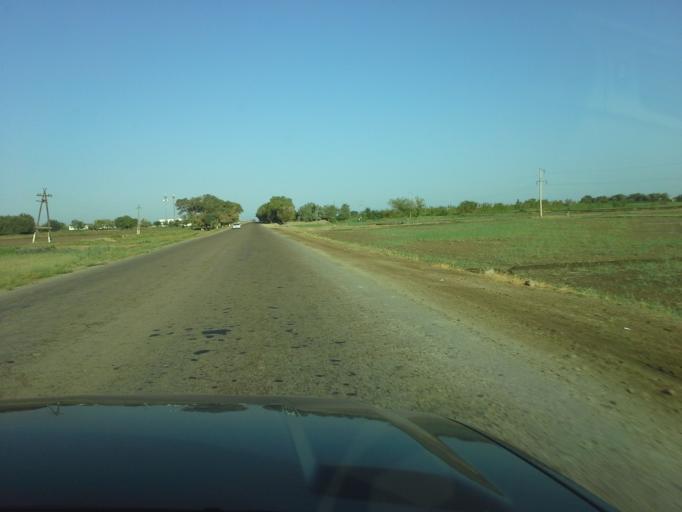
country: UZ
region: Karakalpakstan
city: Khujayli
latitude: 42.2184
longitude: 59.4954
